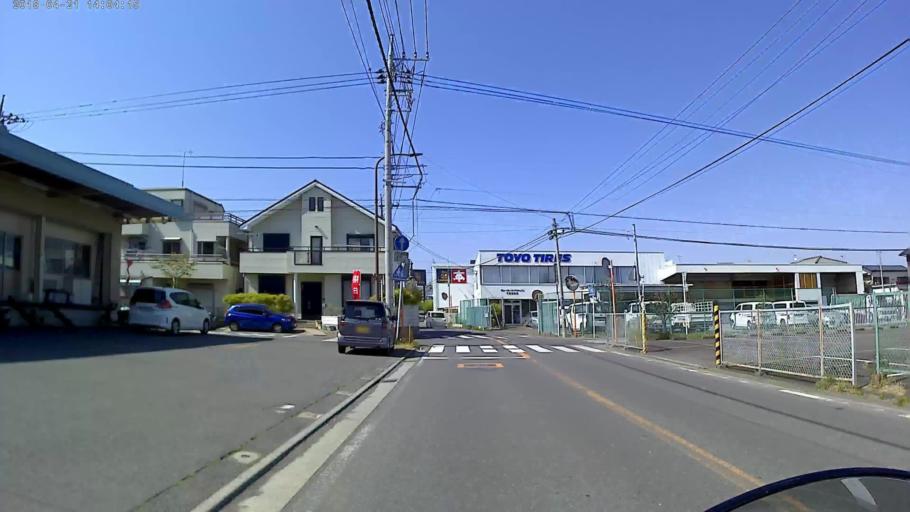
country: JP
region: Kanagawa
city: Hiratsuka
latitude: 35.3495
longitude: 139.3514
